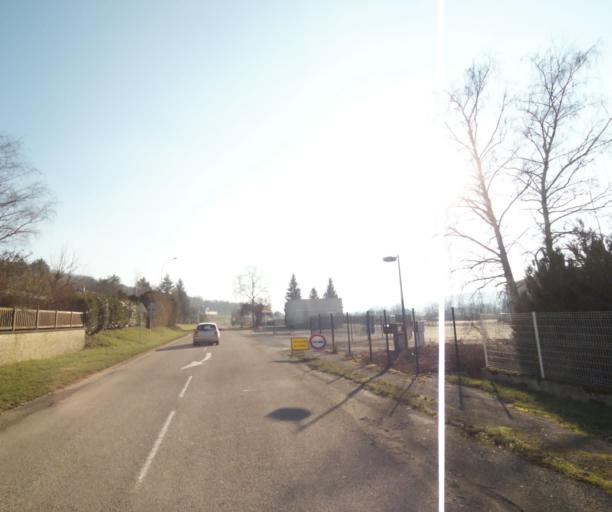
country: FR
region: Champagne-Ardenne
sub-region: Departement de la Haute-Marne
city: Chevillon
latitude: 48.5200
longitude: 5.1177
